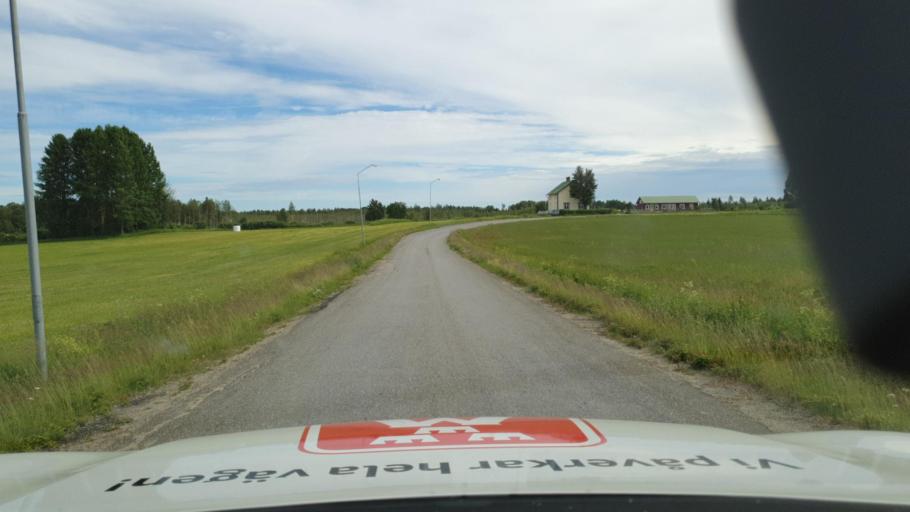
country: SE
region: Vaesterbotten
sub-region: Robertsfors Kommun
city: Robertsfors
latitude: 64.4002
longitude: 21.0203
